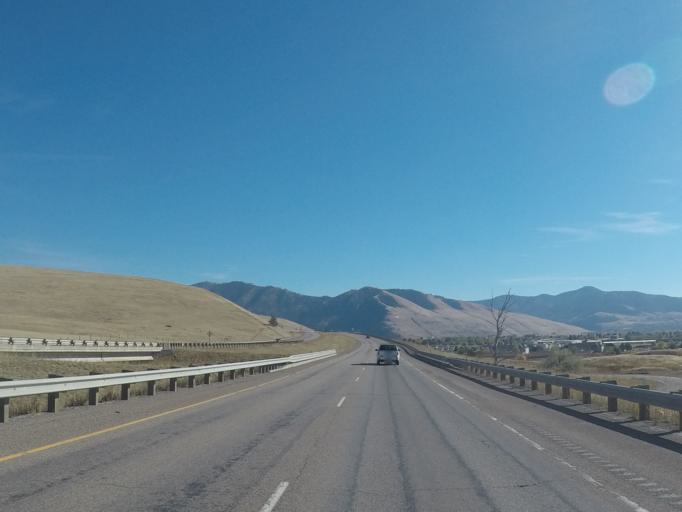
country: US
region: Montana
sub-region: Missoula County
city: Missoula
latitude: 46.8980
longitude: -114.0142
